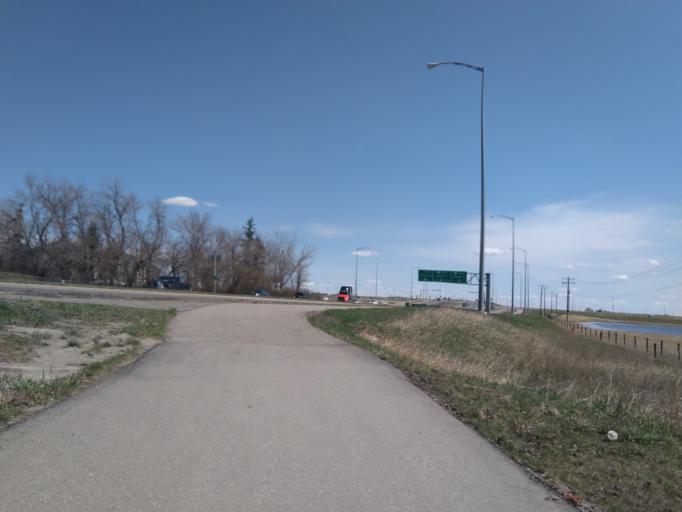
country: CA
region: Alberta
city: Chestermere
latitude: 51.0377
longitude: -113.9296
